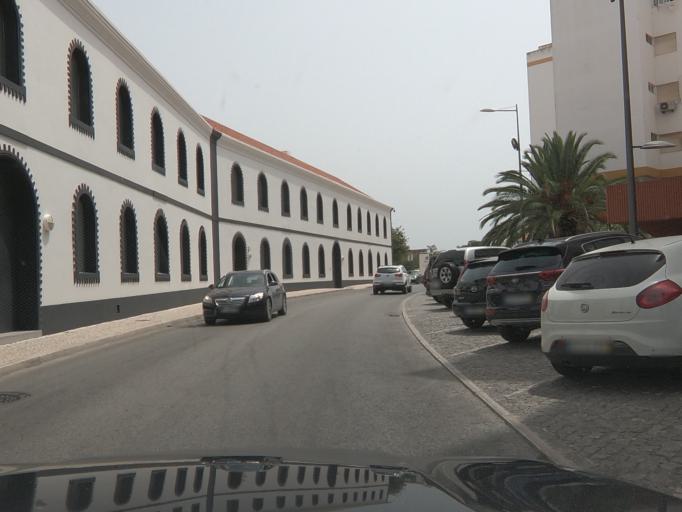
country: PT
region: Faro
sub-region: Portimao
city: Portimao
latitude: 37.1308
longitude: -8.5349
